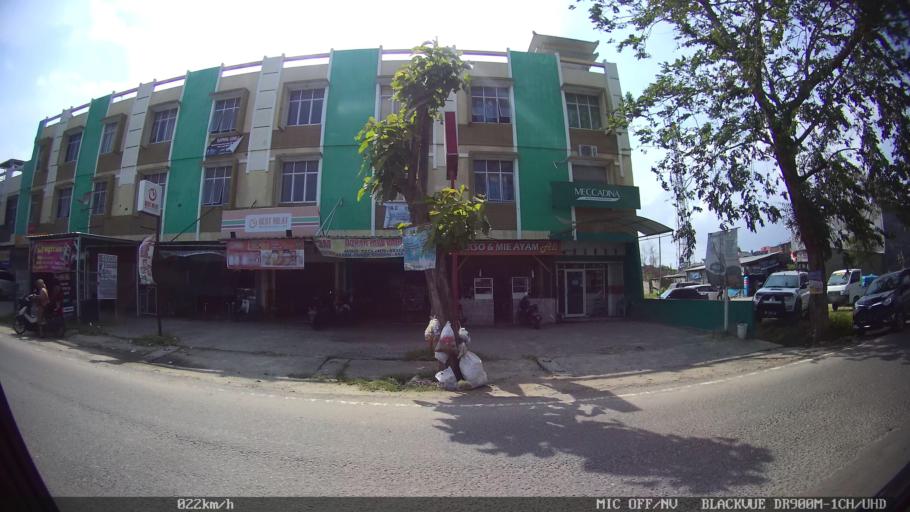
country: ID
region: Lampung
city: Kedaton
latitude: -5.3569
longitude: 105.2615
